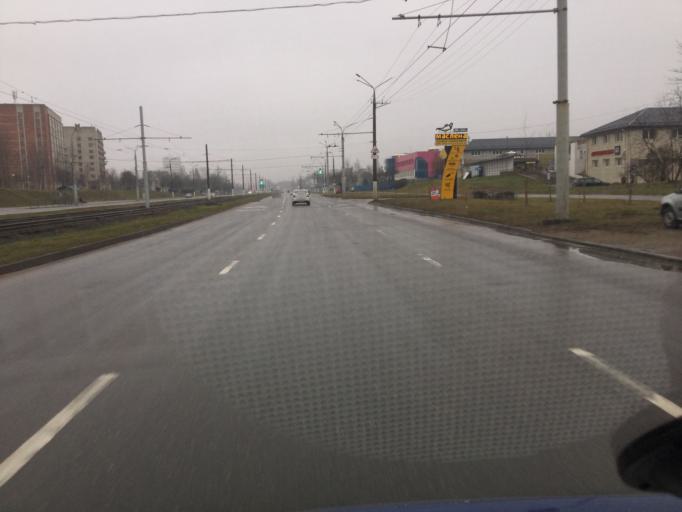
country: BY
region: Vitebsk
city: Vitebsk
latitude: 55.1591
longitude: 30.2351
